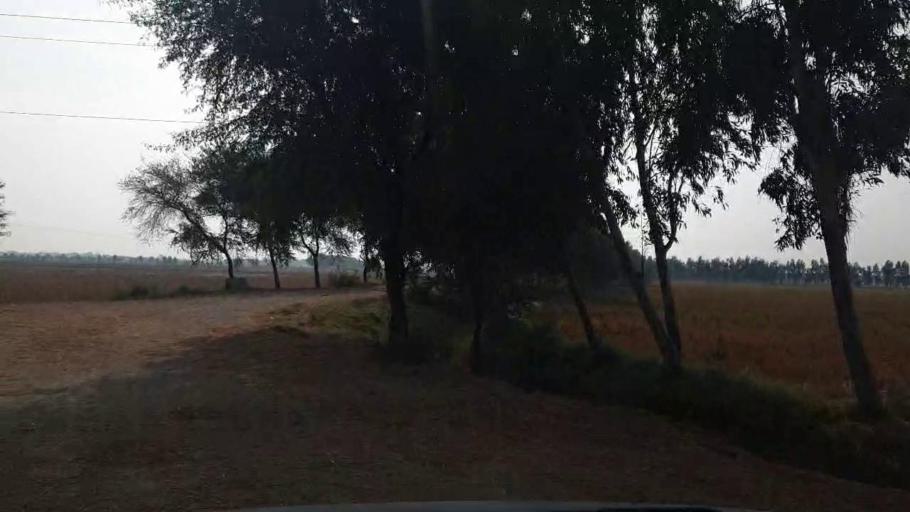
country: PK
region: Sindh
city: Tando Muhammad Khan
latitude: 25.0982
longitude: 68.5026
